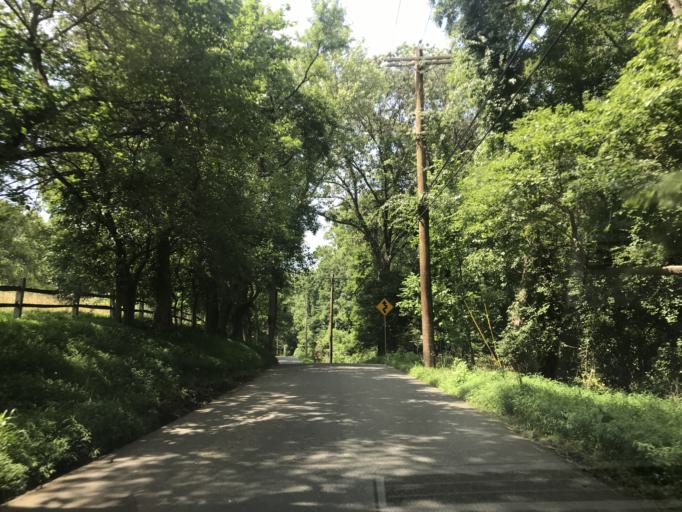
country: US
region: Delaware
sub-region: New Castle County
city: Greenville
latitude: 39.7820
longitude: -75.6433
